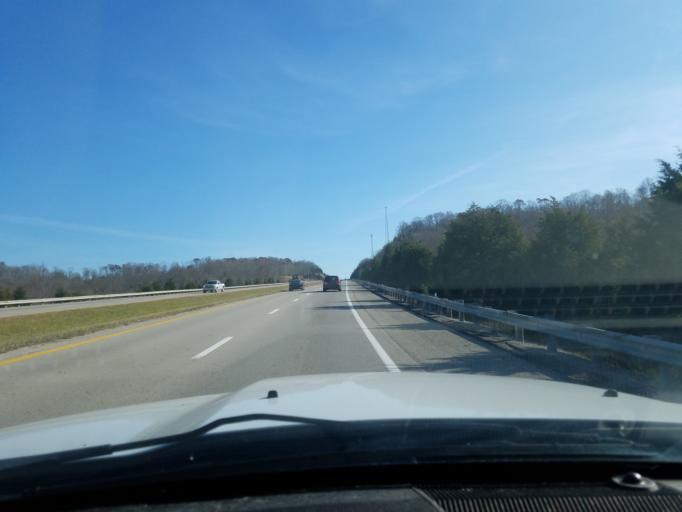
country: US
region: Ohio
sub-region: Adams County
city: Peebles
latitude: 38.9378
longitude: -83.4601
